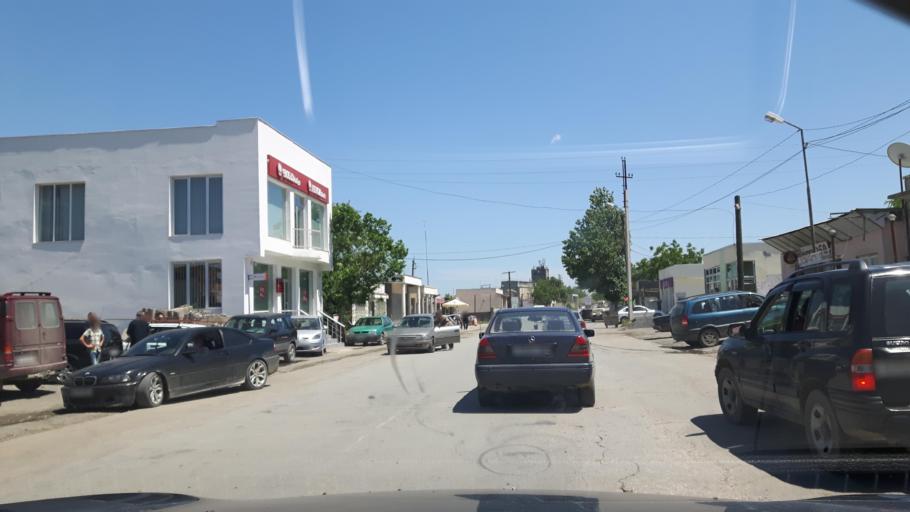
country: GE
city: Tsnori
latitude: 41.6206
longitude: 45.9800
